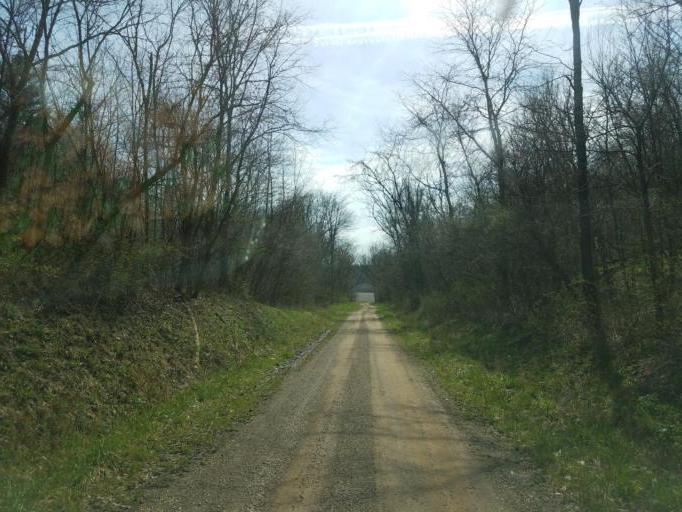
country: US
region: Ohio
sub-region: Knox County
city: Oak Hill
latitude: 40.3710
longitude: -82.1617
